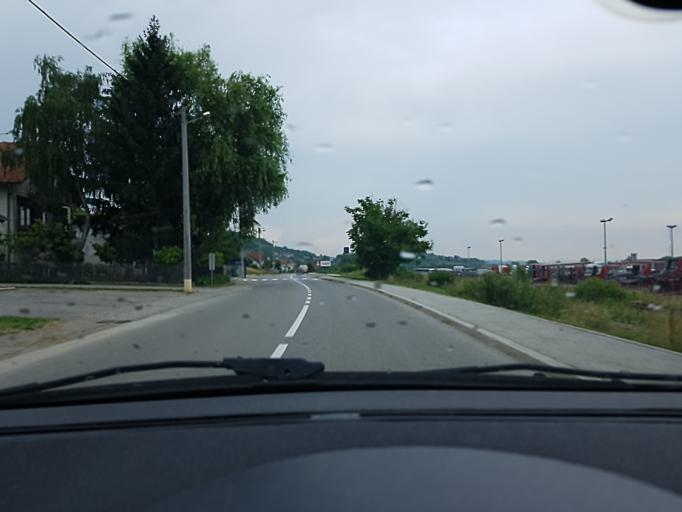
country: HR
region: Zagrebacka
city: Pojatno
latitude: 45.9120
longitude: 15.8081
